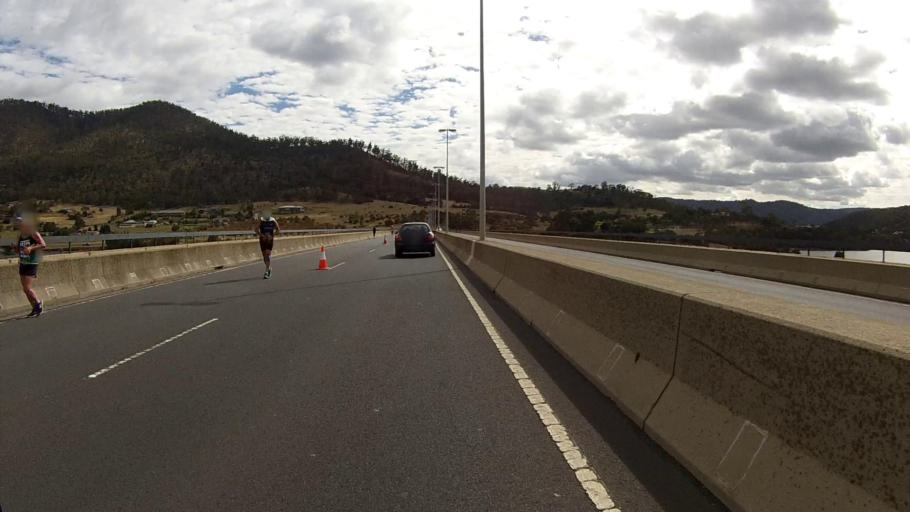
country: AU
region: Tasmania
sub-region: Glenorchy
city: Lutana
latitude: -42.8166
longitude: 147.3083
